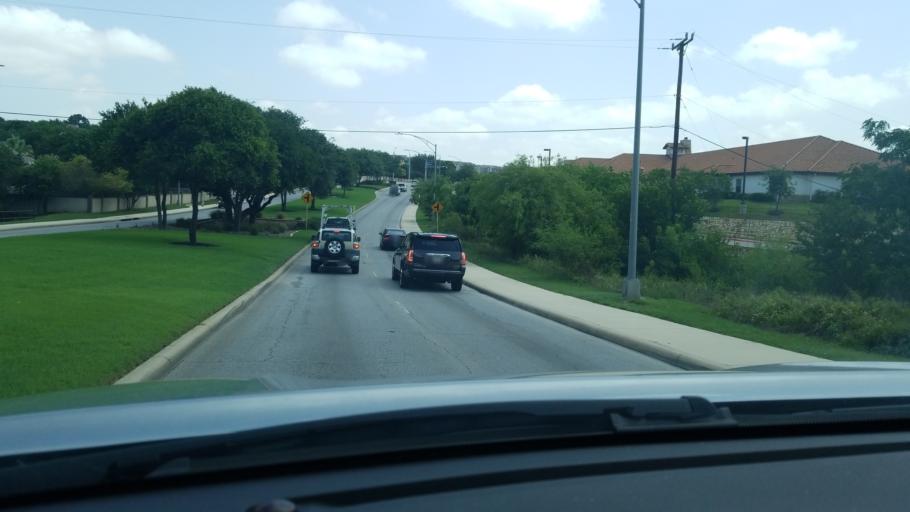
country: US
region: Texas
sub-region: Bexar County
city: Hollywood Park
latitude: 29.6372
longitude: -98.4954
